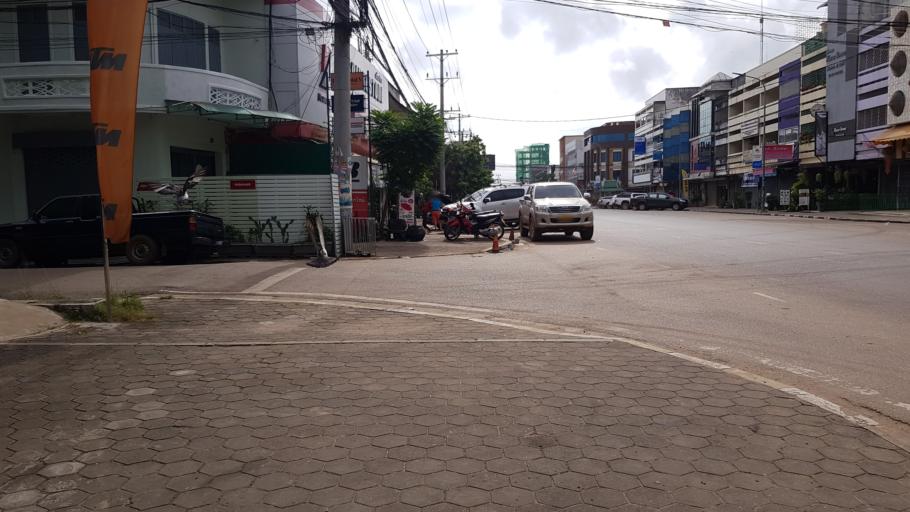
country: LA
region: Vientiane
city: Vientiane
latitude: 17.9693
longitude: 102.6022
